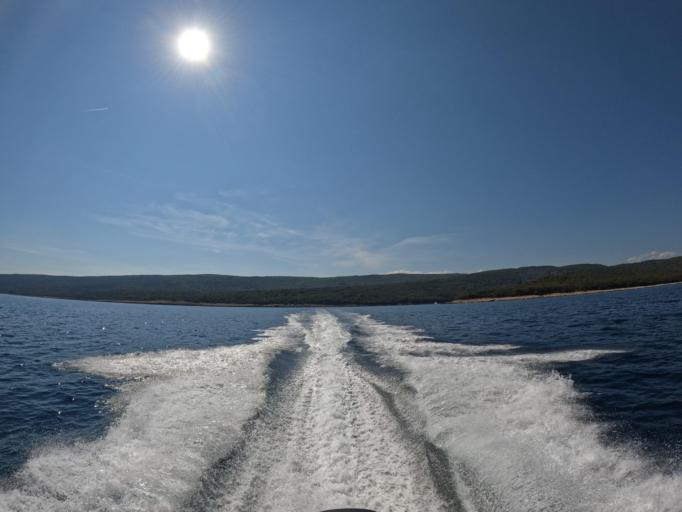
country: HR
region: Primorsko-Goranska
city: Cres
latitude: 44.9462
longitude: 14.4752
